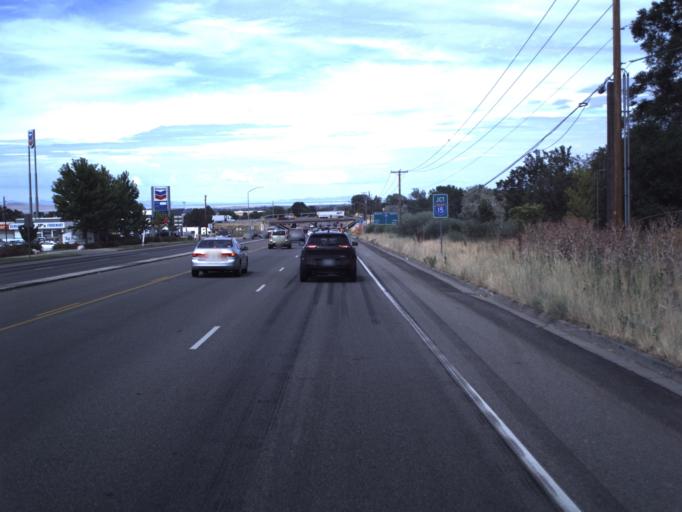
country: US
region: Utah
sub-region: Davis County
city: Hill Air Force Bace
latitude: 41.1036
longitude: -111.9981
